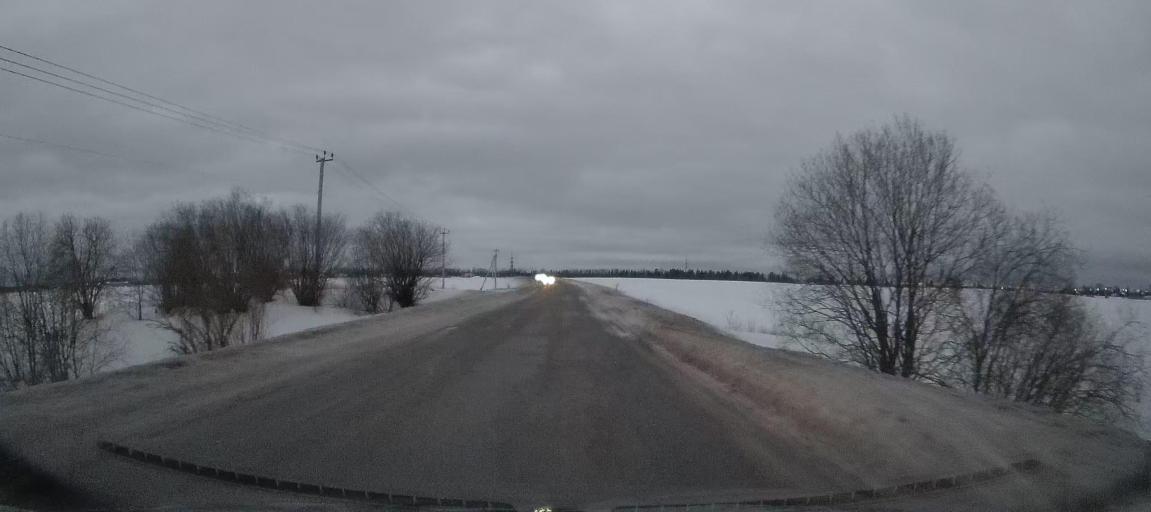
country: RU
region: Leningrad
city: Taytsy
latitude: 59.6870
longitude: 30.1255
